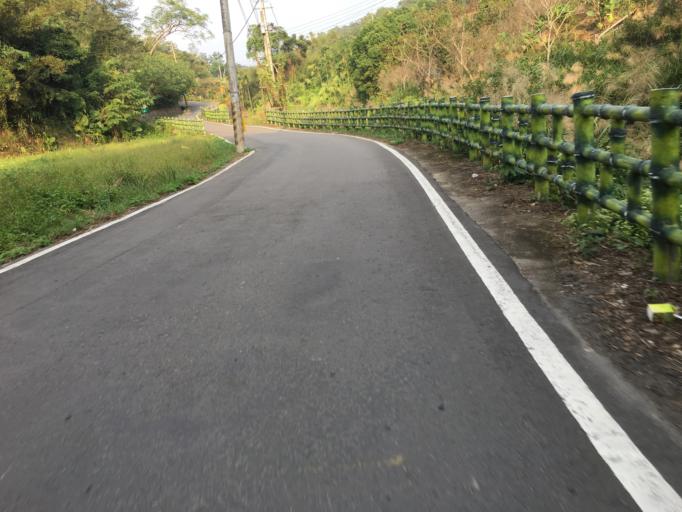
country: TW
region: Taiwan
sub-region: Hsinchu
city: Hsinchu
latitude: 24.7075
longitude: 121.0555
